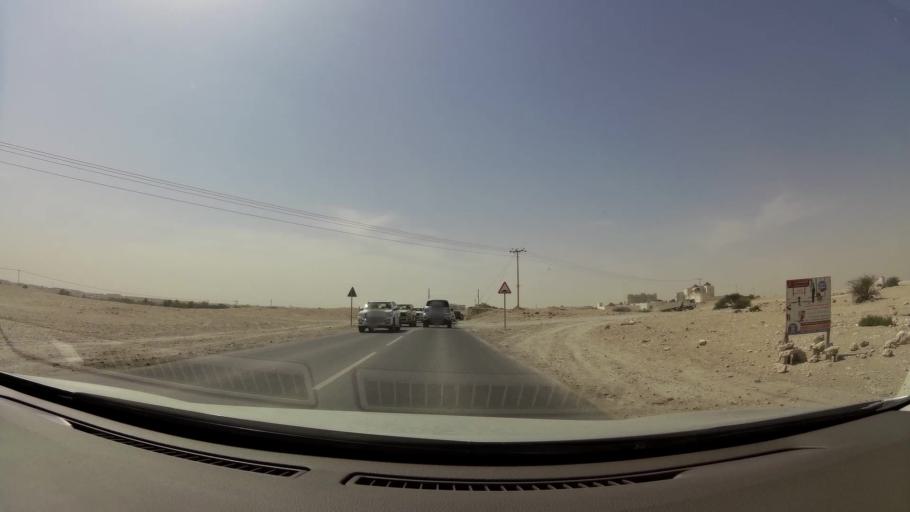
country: QA
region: Baladiyat ar Rayyan
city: Ar Rayyan
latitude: 25.2643
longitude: 51.4023
